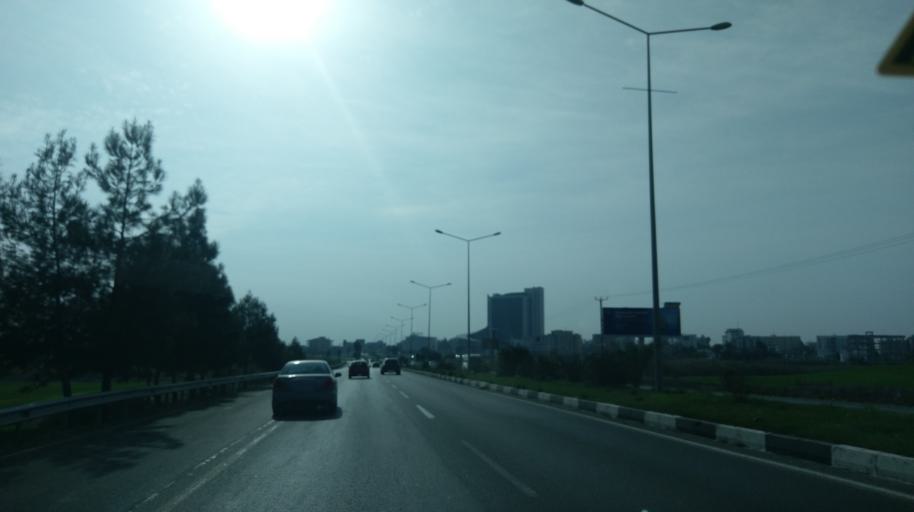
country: CY
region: Lefkosia
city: Nicosia
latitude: 35.2148
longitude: 33.3204
